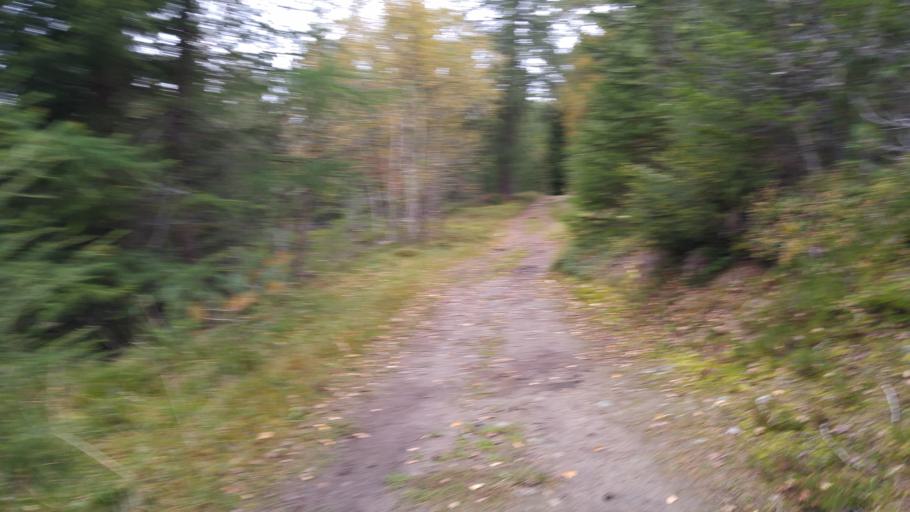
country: NO
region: Sor-Trondelag
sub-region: Trondheim
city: Trondheim
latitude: 63.4230
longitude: 10.3212
